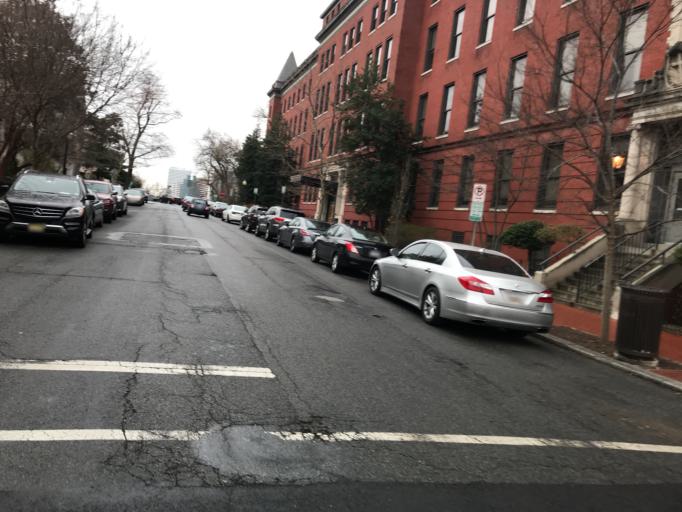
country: US
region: Washington, D.C.
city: Washington, D.C.
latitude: 38.9068
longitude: -77.0689
